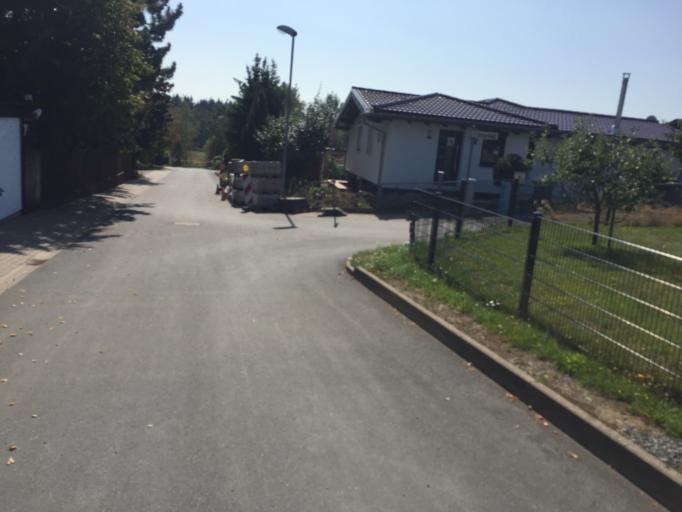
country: DE
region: Hesse
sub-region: Regierungsbezirk Darmstadt
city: Butzbach
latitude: 50.4220
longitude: 8.5914
